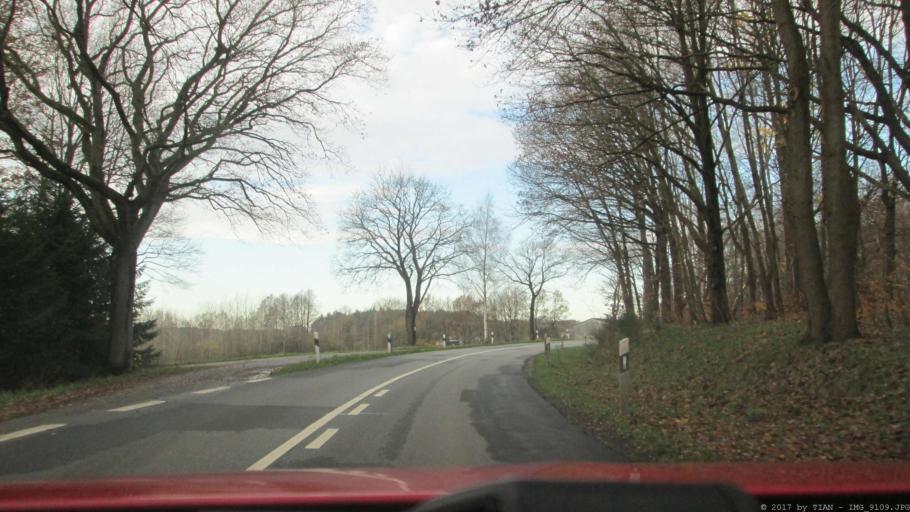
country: DE
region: Lower Saxony
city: Hankensbuttel
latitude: 52.7084
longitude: 10.6301
